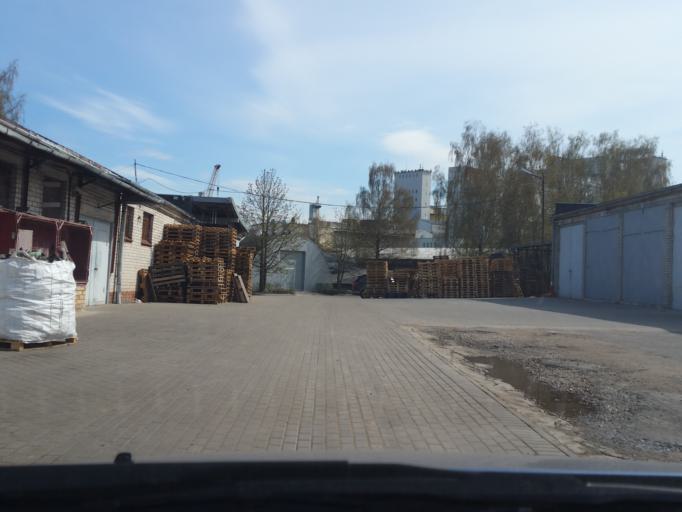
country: LV
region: Riga
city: Jaunciems
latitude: 56.9906
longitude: 24.1959
